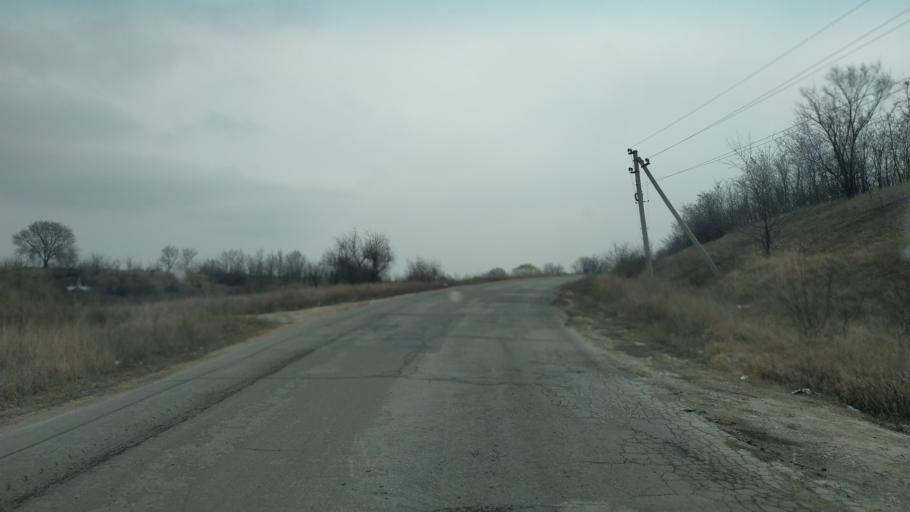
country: MD
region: Chisinau
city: Singera
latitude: 46.9158
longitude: 28.9881
